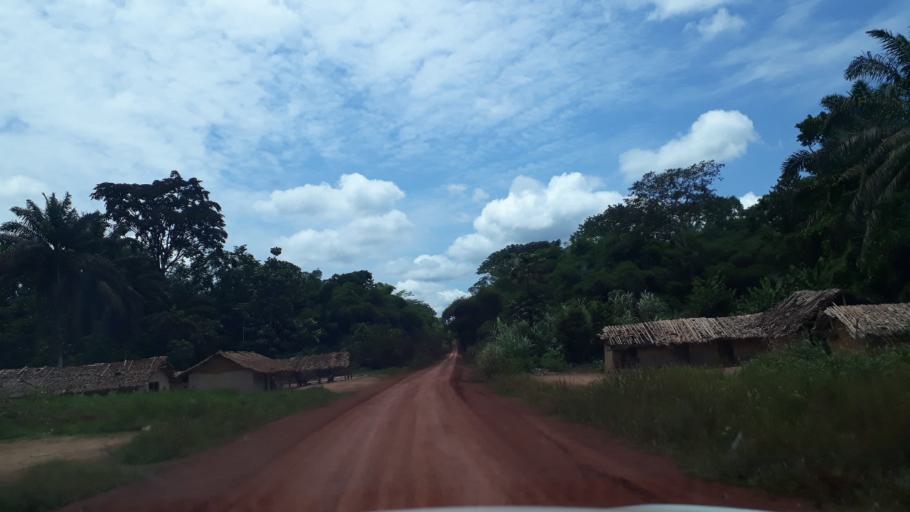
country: CD
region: Eastern Province
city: Kisangani
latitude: 0.5463
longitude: 25.8314
